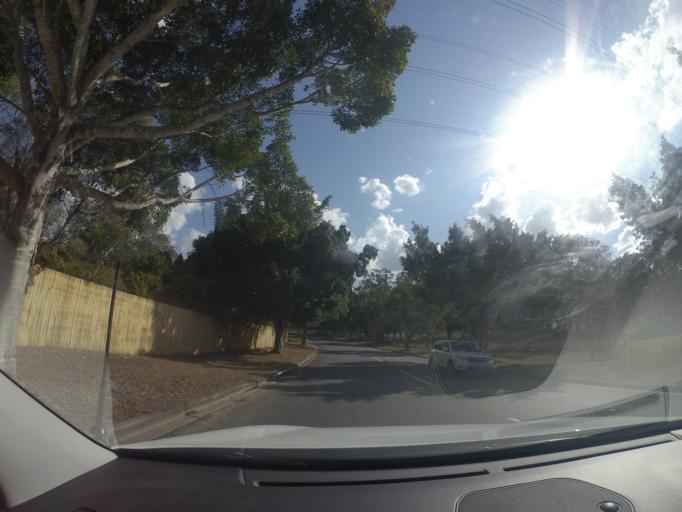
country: AU
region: Queensland
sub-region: Logan
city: Woodridge
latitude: -27.6509
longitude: 153.0650
